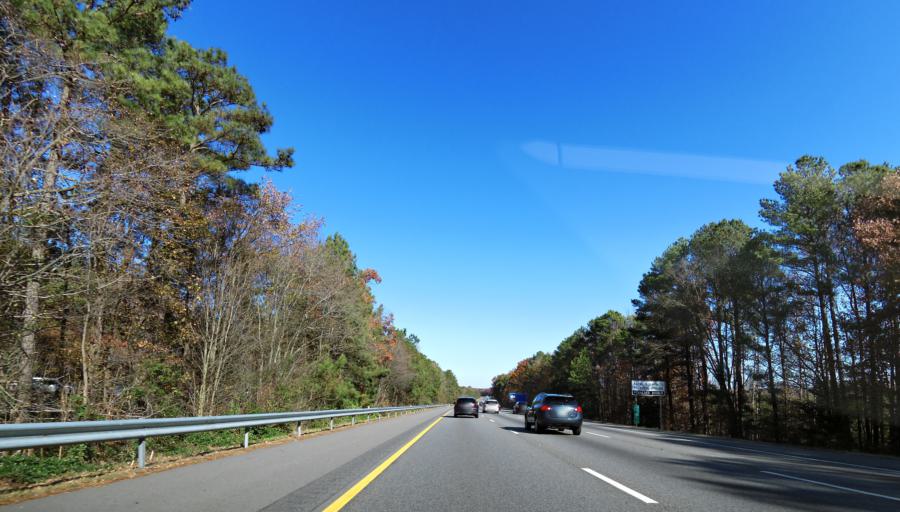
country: US
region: Virginia
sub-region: Hanover County
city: Ashland
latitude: 37.8208
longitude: -77.4573
